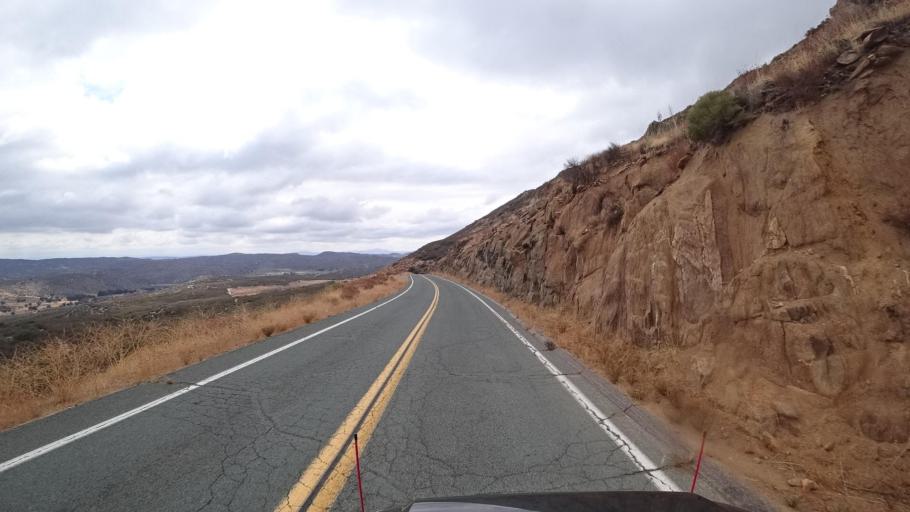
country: US
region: California
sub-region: San Diego County
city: Pine Valley
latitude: 32.7442
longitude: -116.4527
